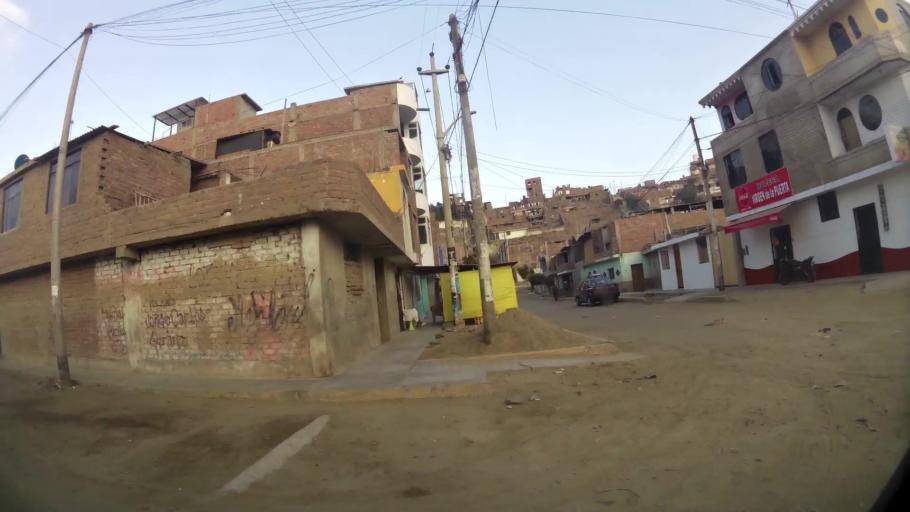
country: PE
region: La Libertad
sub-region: Provincia de Trujillo
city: El Porvenir
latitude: -8.0813
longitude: -79.0070
